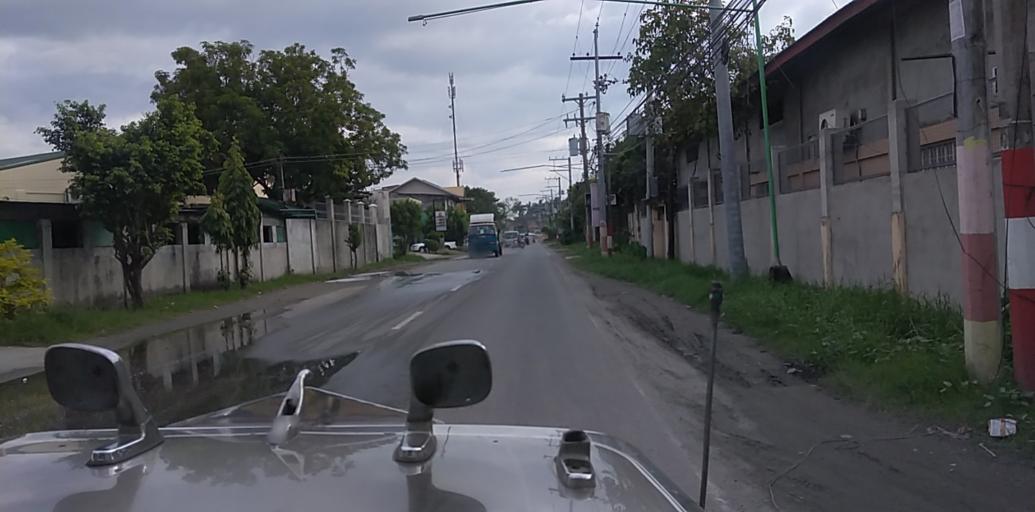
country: PH
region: Central Luzon
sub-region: Province of Pampanga
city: Minalin
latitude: 14.9908
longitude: 120.7044
